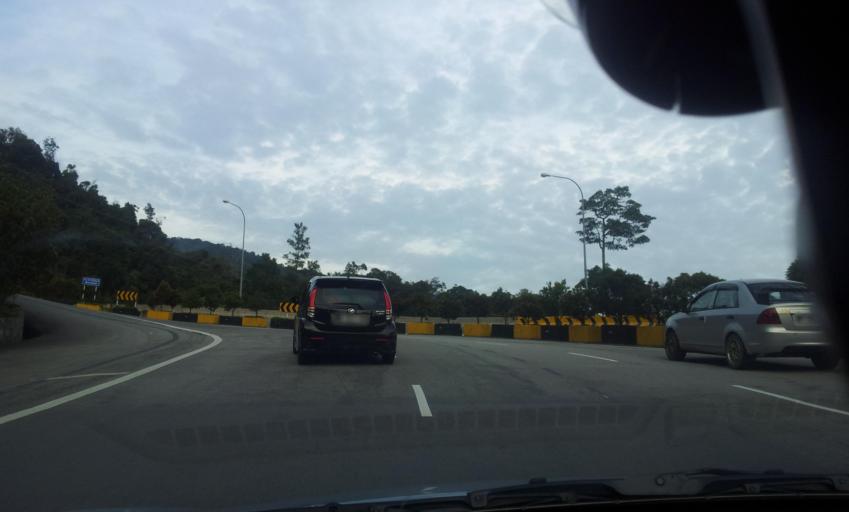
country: MY
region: Pahang
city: Kampung Bukit Tinggi, Bentong
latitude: 3.4103
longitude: 101.7833
